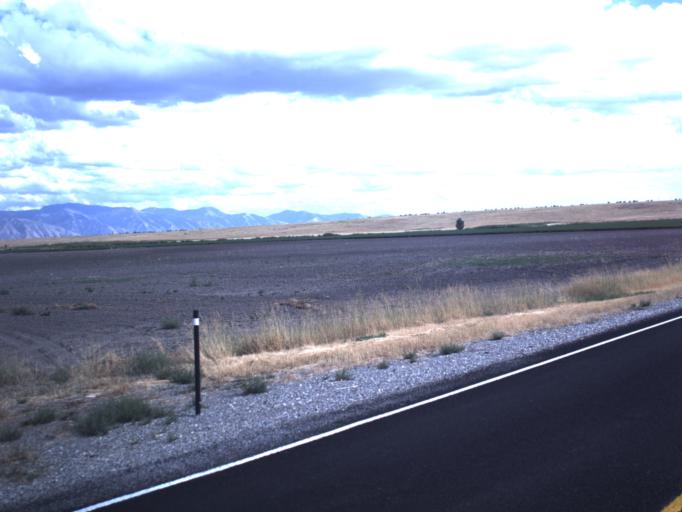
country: US
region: Utah
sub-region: Cache County
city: Benson
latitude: 41.9043
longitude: -112.0457
